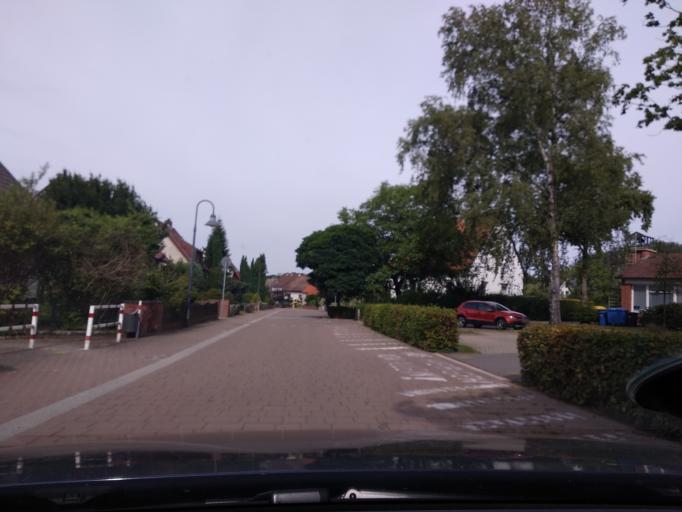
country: DE
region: Lower Saxony
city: Wagenhoff
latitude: 52.5115
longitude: 10.4732
